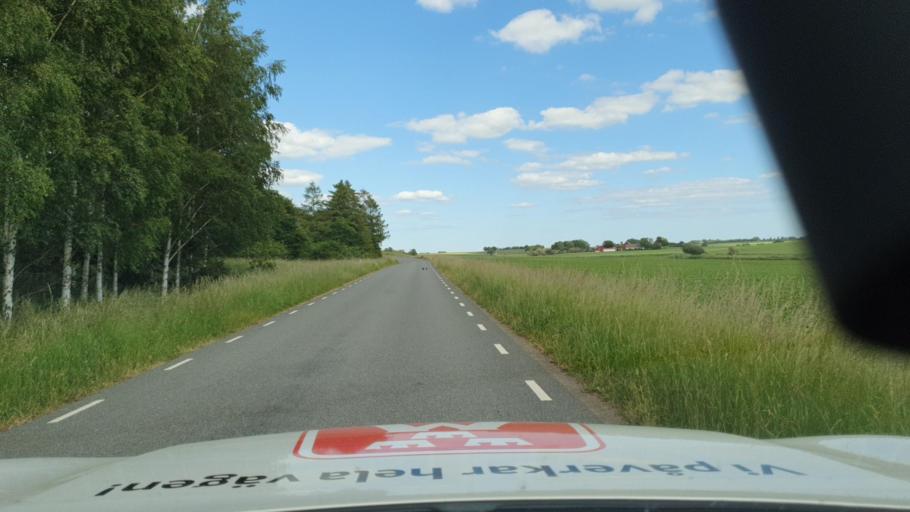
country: SE
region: Skane
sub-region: Ystads Kommun
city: Kopingebro
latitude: 55.4778
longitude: 14.0125
